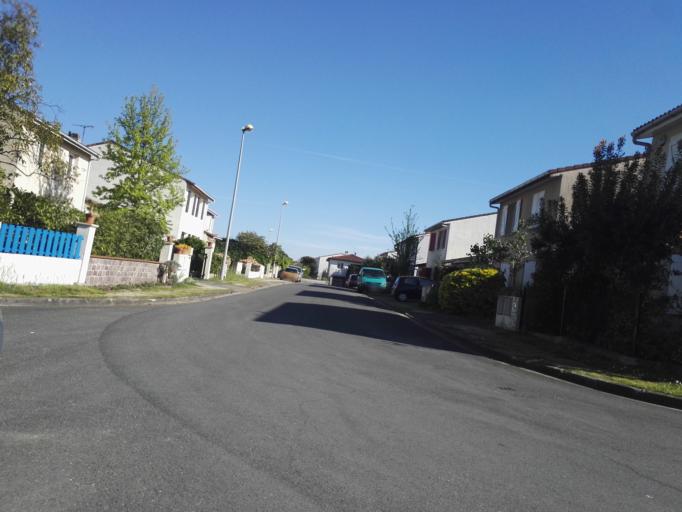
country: FR
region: Aquitaine
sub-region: Departement de la Gironde
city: Talence
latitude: 44.7963
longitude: -0.5840
